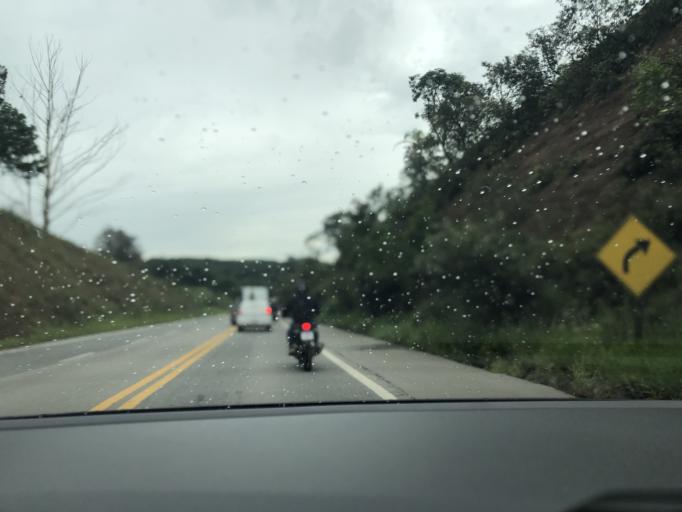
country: BR
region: Sao Paulo
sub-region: Jarinu
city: Jarinu
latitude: -23.1274
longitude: -46.7363
